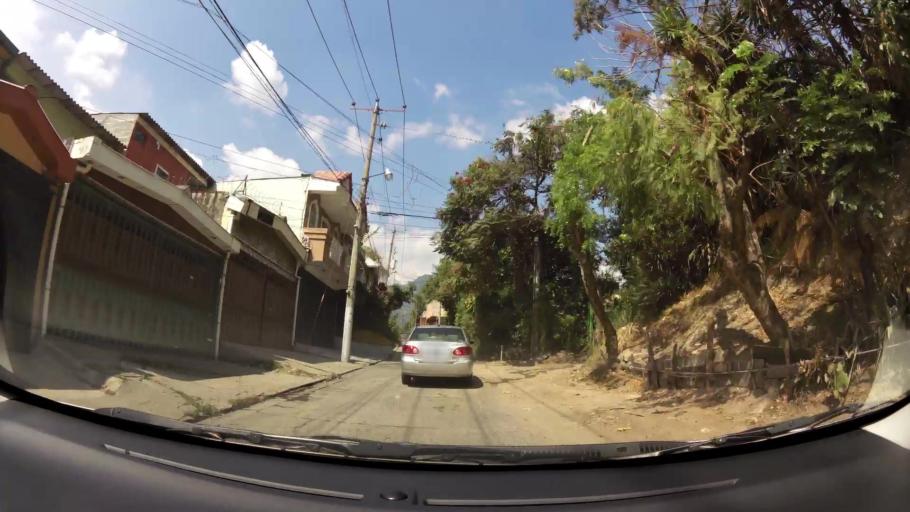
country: SV
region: San Salvador
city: Mejicanos
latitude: 13.7085
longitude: -89.2230
